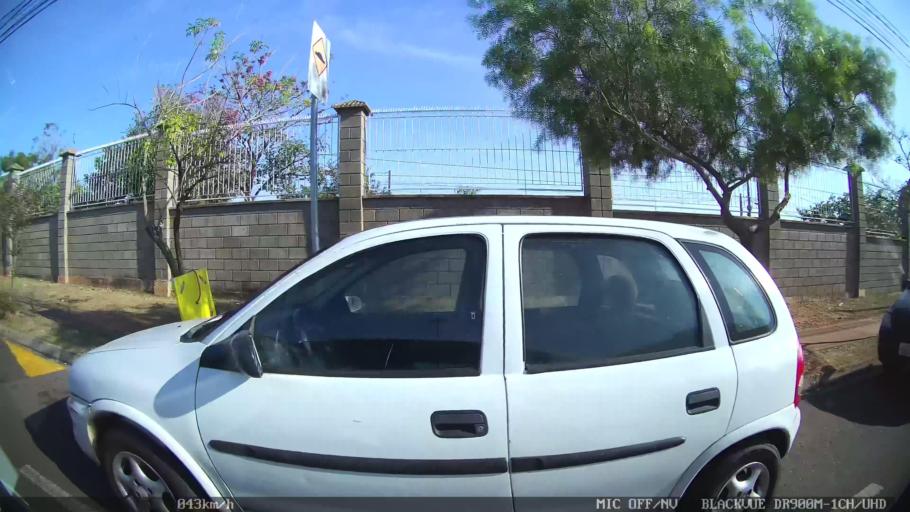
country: BR
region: Sao Paulo
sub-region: Sao Jose Do Rio Preto
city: Sao Jose do Rio Preto
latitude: -20.7720
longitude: -49.3325
